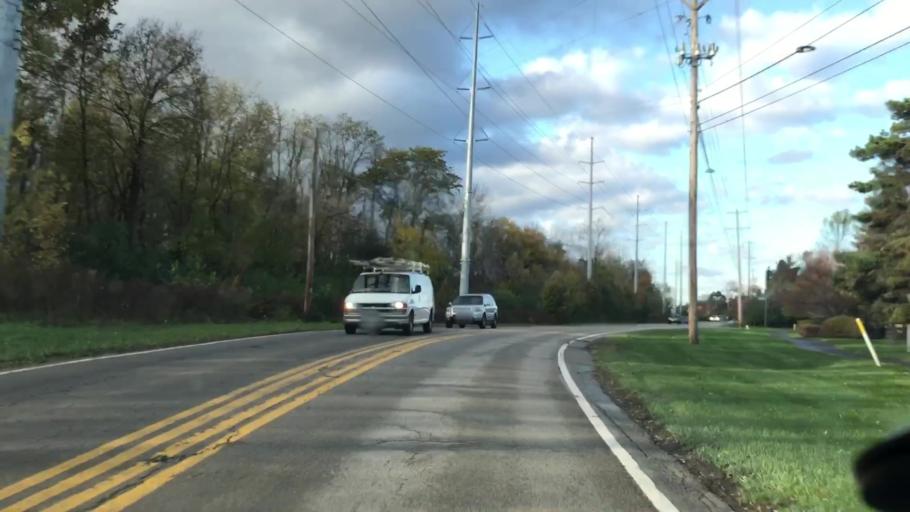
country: US
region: Ohio
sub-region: Franklin County
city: Upper Arlington
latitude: 40.0140
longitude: -83.1042
